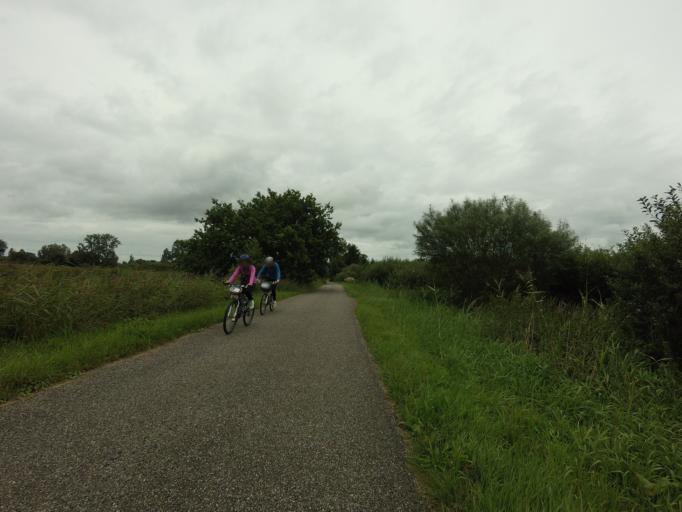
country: NL
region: Friesland
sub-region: Gemeente Weststellingwerf
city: Wolvega
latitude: 52.8634
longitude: 6.0351
